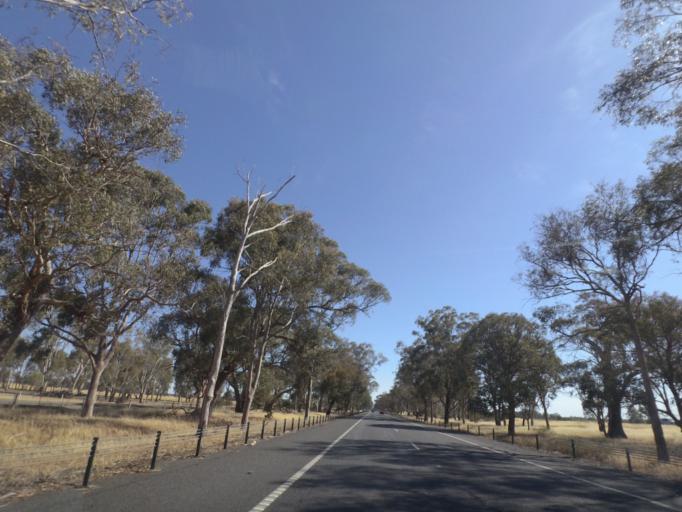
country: AU
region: Victoria
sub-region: Greater Shepparton
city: Shepparton
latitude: -36.5792
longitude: 145.3394
